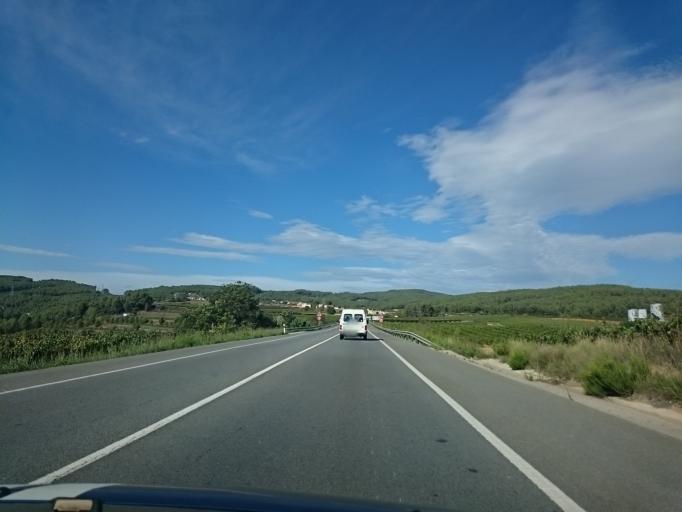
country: ES
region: Catalonia
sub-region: Provincia de Barcelona
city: Subirats
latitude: 41.3764
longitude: 1.8078
